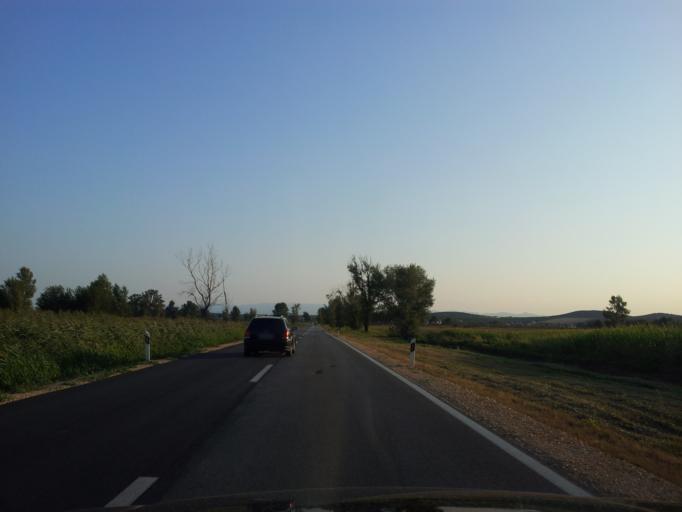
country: HR
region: Zadarska
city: Biograd na Moru
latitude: 43.9704
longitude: 15.4844
